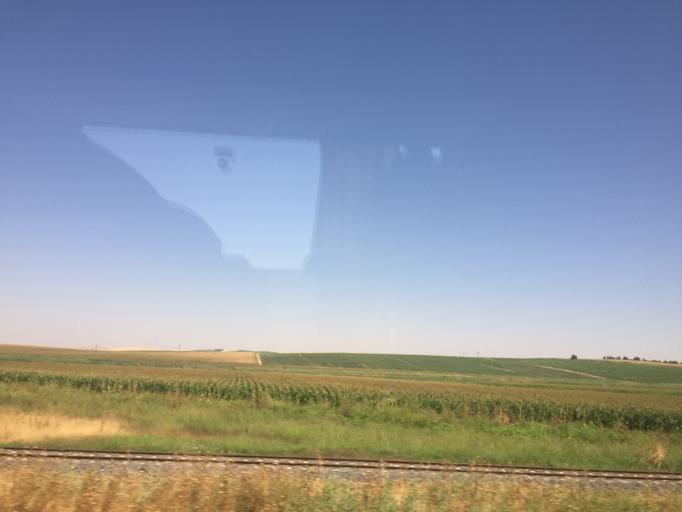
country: TR
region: Diyarbakir
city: Tepe
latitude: 37.8505
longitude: 40.7429
